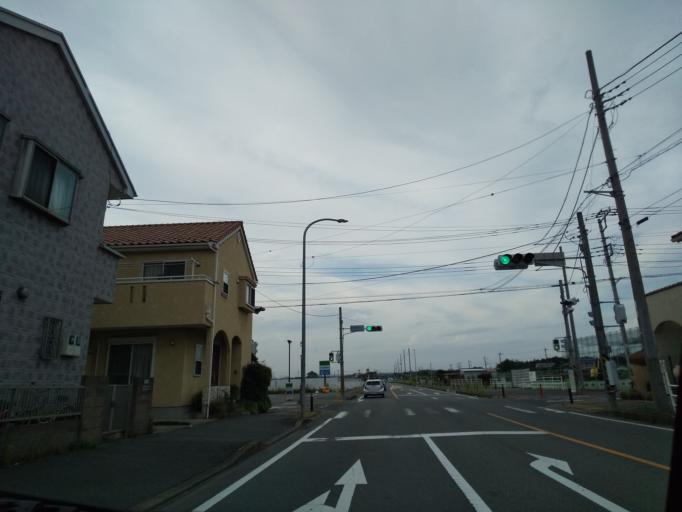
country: JP
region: Kanagawa
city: Atsugi
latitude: 35.4692
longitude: 139.3589
